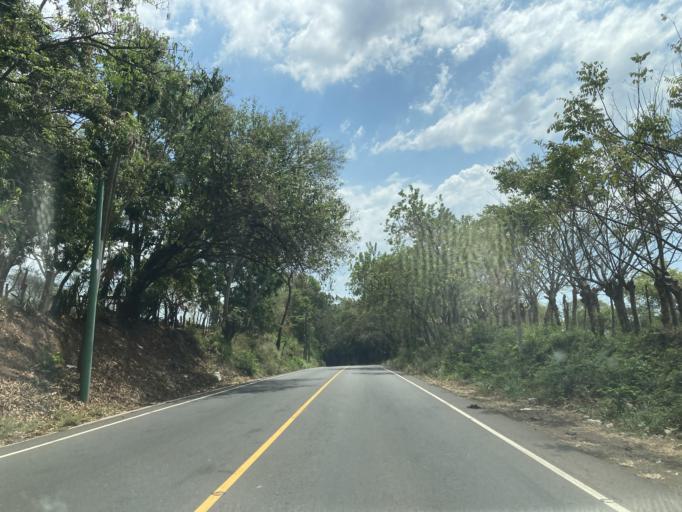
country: GT
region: Santa Rosa
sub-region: Municipio de Taxisco
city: Taxisco
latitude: 14.0765
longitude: -90.4810
